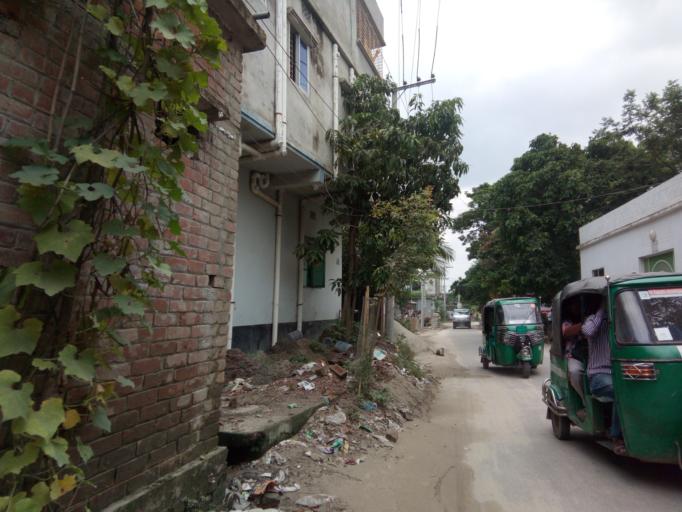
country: BD
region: Dhaka
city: Azimpur
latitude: 23.7353
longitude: 90.3484
